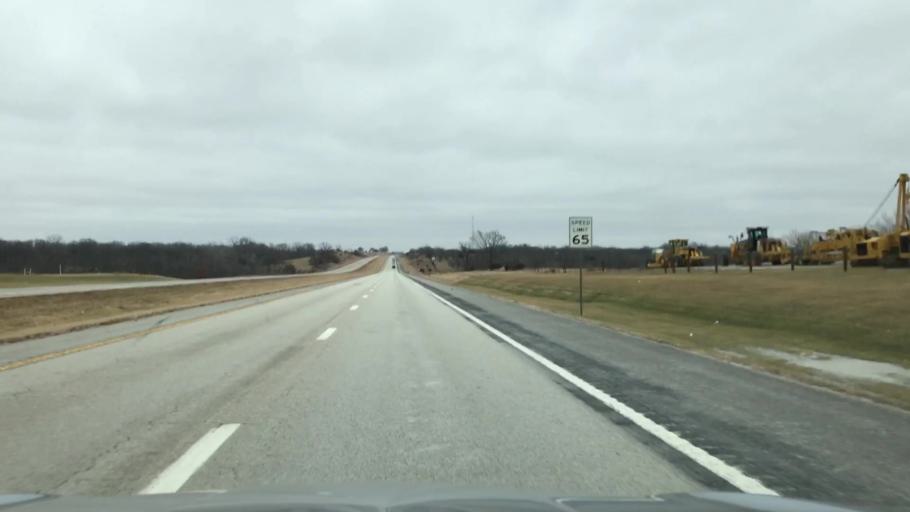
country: US
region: Missouri
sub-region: Caldwell County
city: Hamilton
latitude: 39.7493
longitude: -94.0764
